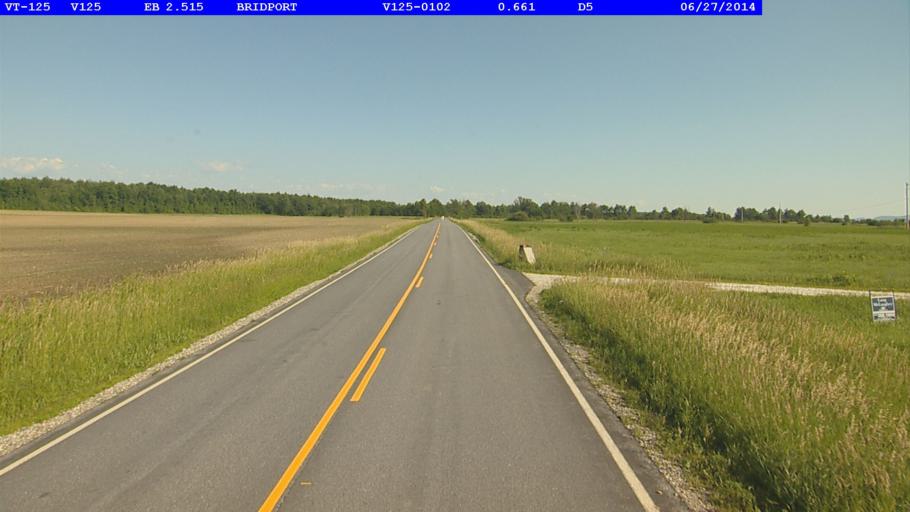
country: US
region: New York
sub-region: Essex County
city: Port Henry
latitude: 44.0126
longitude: -73.3885
